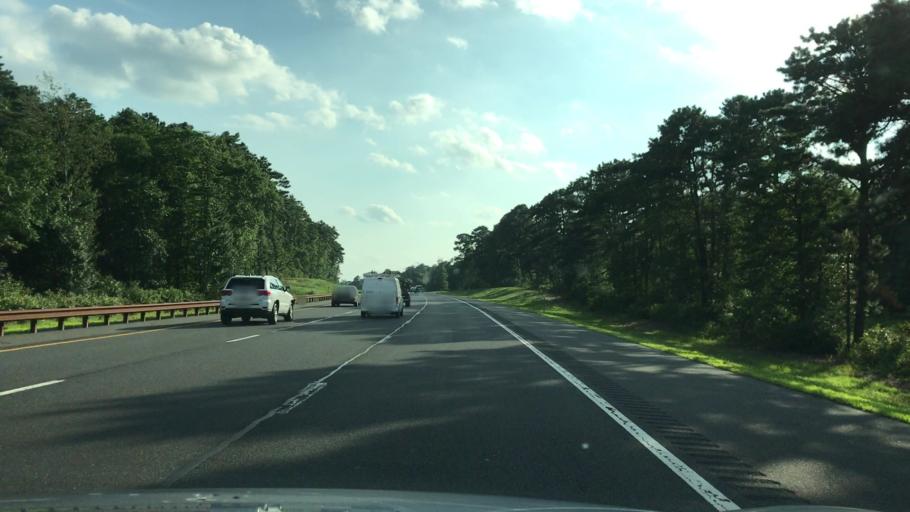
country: US
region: New Jersey
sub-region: Ocean County
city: Tuckerton
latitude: 39.6352
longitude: -74.3788
